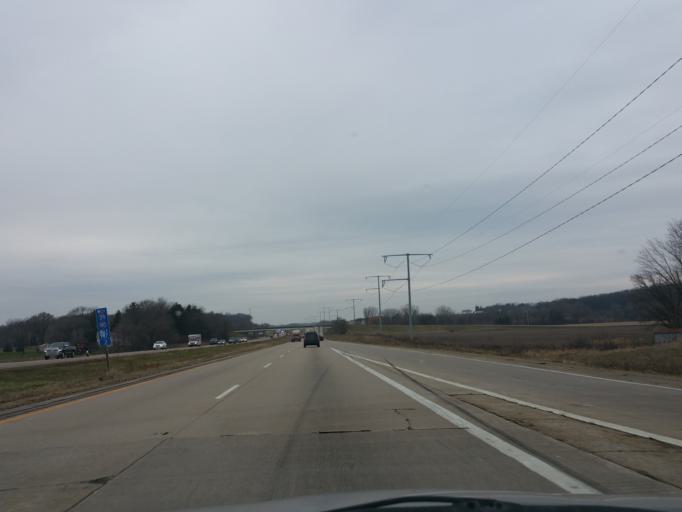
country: US
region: Wisconsin
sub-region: Dane County
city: Cottage Grove
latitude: 43.0032
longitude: -89.2047
